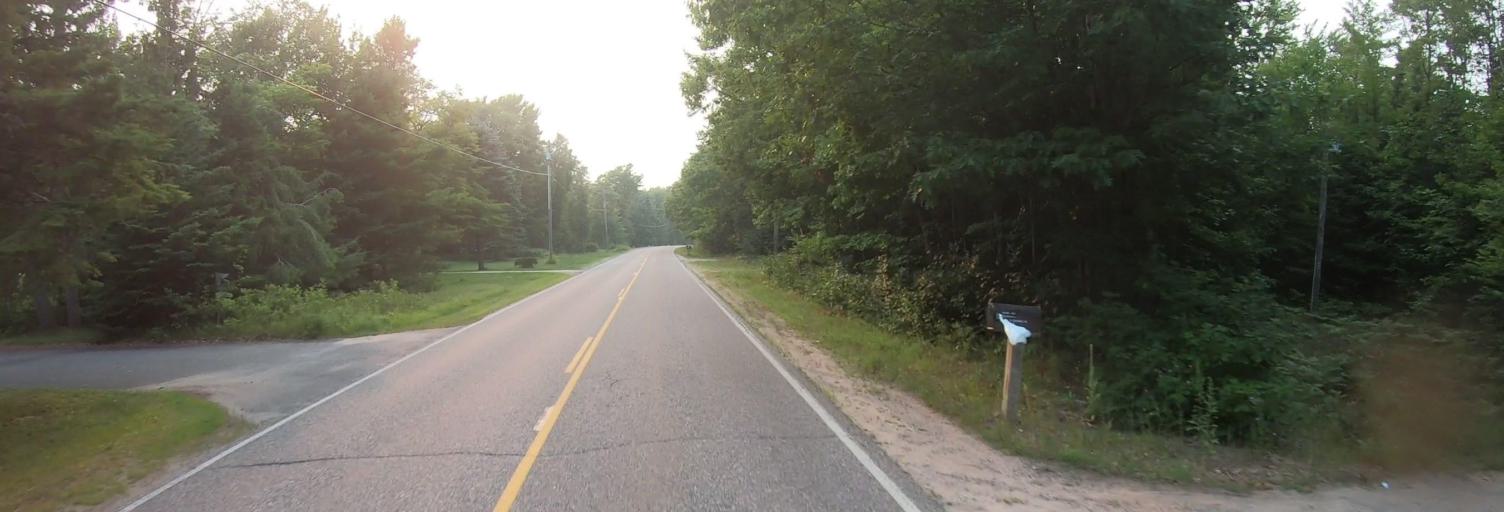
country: US
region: Michigan
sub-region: Chippewa County
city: Sault Ste. Marie
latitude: 46.4822
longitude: -84.6621
